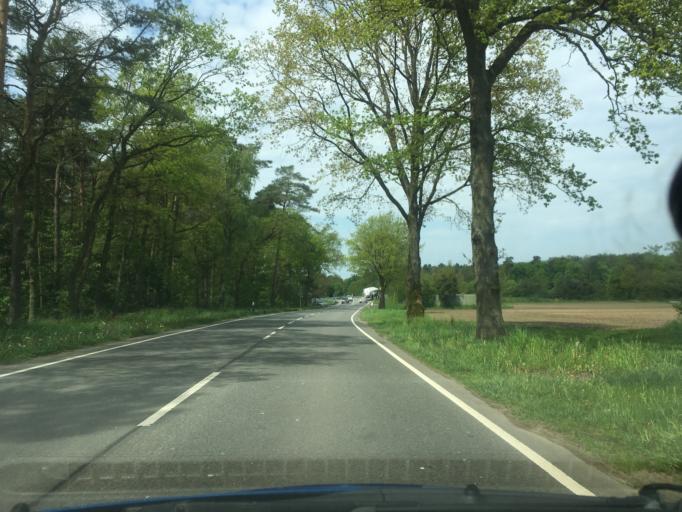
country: DE
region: Lower Saxony
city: Deutsch Evern
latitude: 53.2114
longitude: 10.4437
